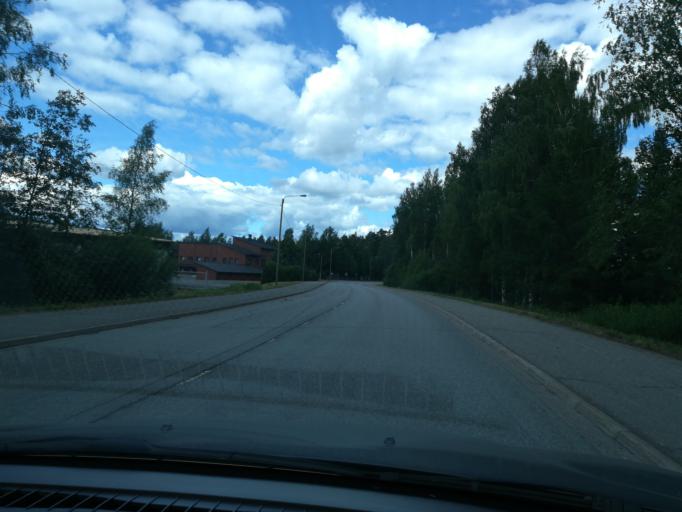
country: FI
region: Southern Savonia
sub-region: Mikkeli
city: Maentyharju
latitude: 61.4119
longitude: 26.8838
